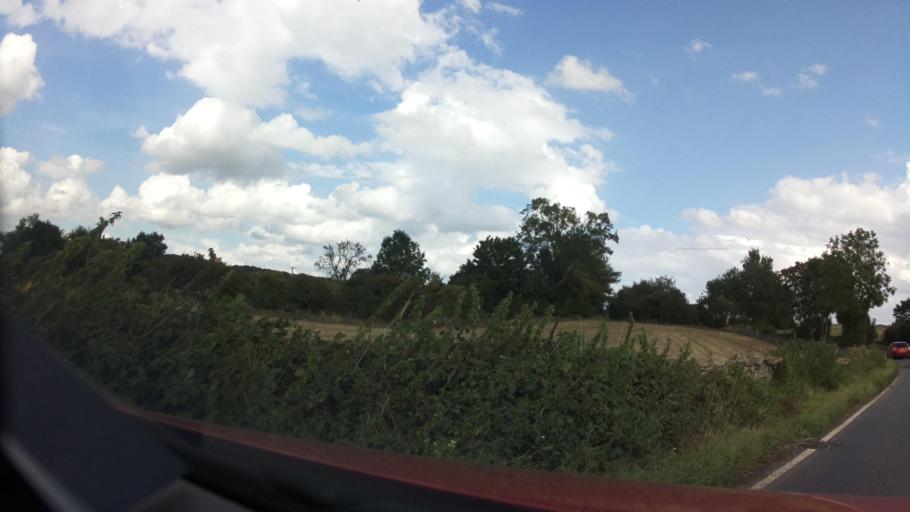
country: GB
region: England
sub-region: North Yorkshire
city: Leyburn
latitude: 54.2826
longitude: -1.7903
